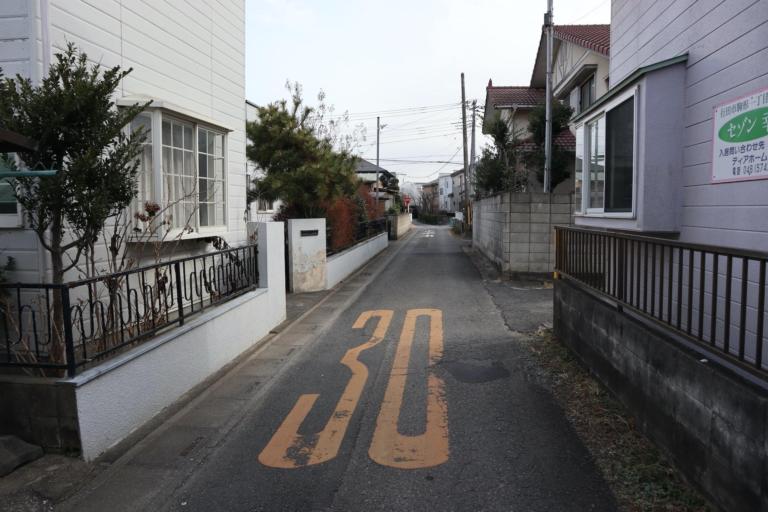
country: JP
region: Saitama
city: Gyoda
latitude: 36.1295
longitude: 139.4563
